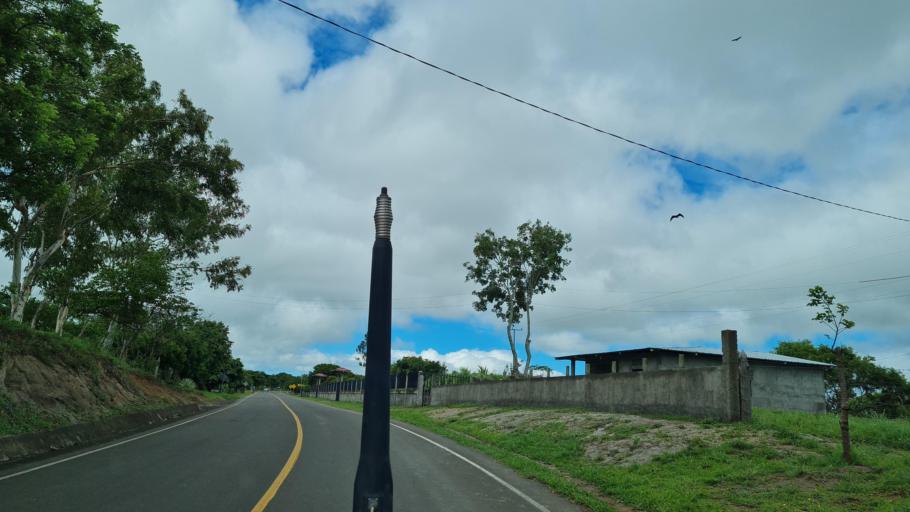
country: NI
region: Matagalpa
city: Terrabona
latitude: 12.5921
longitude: -85.9578
